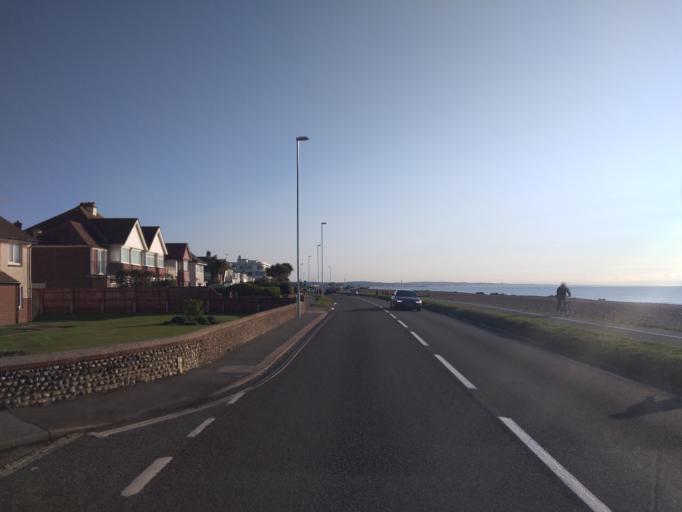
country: GB
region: England
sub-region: West Sussex
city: Lancing
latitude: 50.8146
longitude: -0.3449
